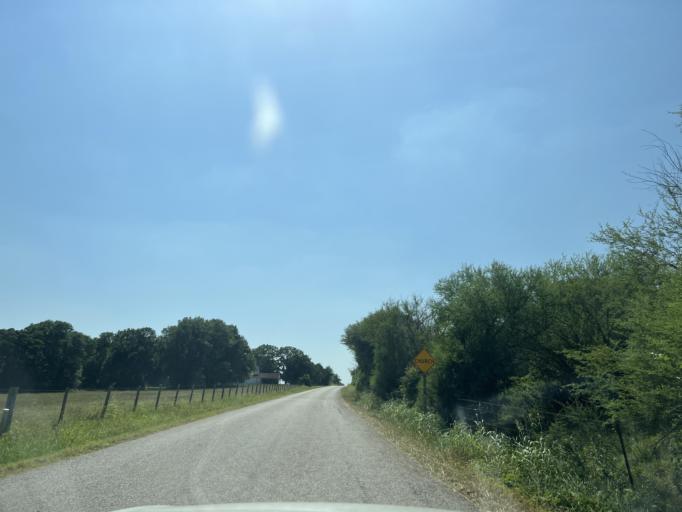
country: US
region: Texas
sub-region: Washington County
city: Brenham
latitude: 30.1533
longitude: -96.4767
